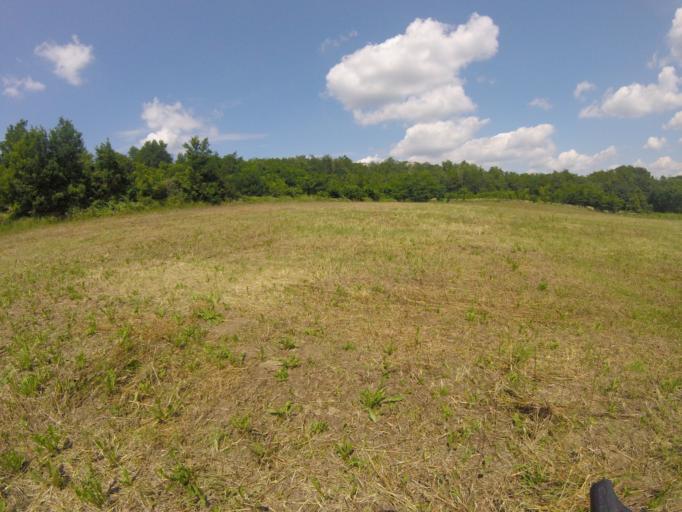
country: HU
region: Zala
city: Nagykanizsa
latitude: 46.5562
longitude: 17.0279
